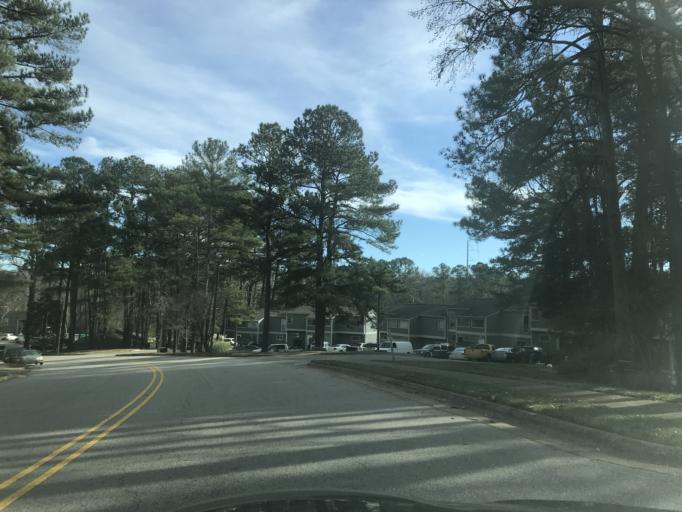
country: US
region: North Carolina
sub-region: Wake County
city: Cary
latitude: 35.7743
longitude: -78.7402
